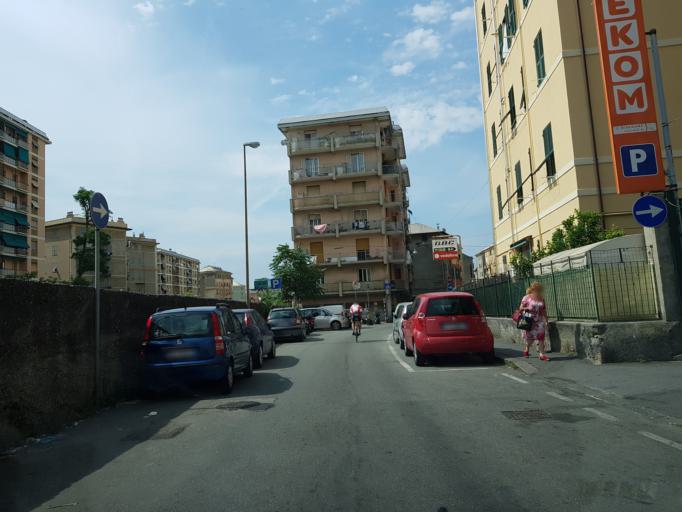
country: IT
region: Liguria
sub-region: Provincia di Genova
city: San Teodoro
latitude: 44.4279
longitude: 8.8540
